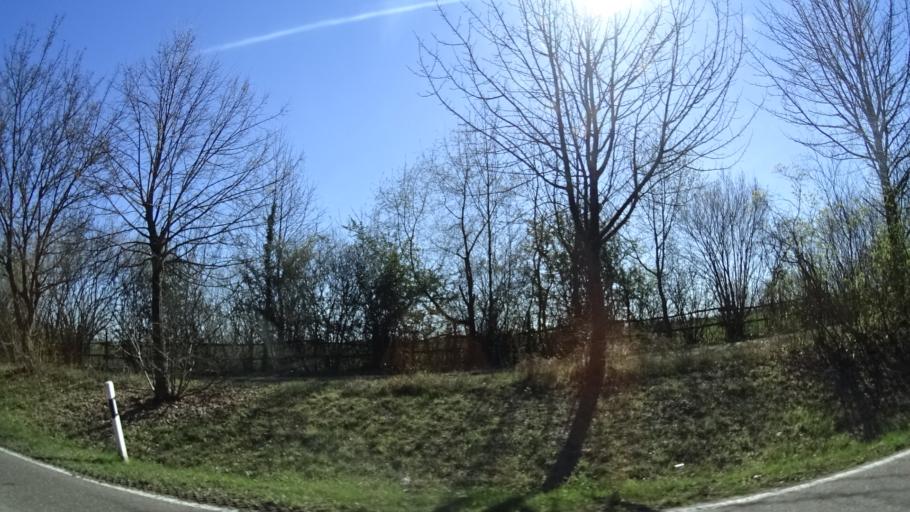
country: DE
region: Rheinland-Pfalz
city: Dolgesheim
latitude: 49.7912
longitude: 8.2588
